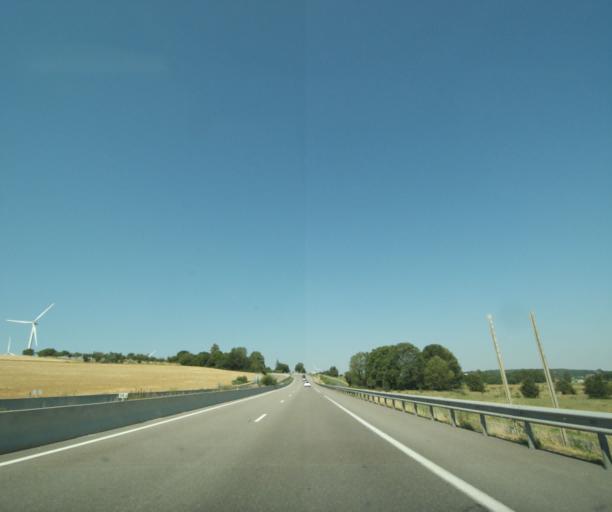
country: FR
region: Lorraine
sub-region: Departement de la Meuse
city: Lerouville
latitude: 48.7054
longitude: 5.4532
